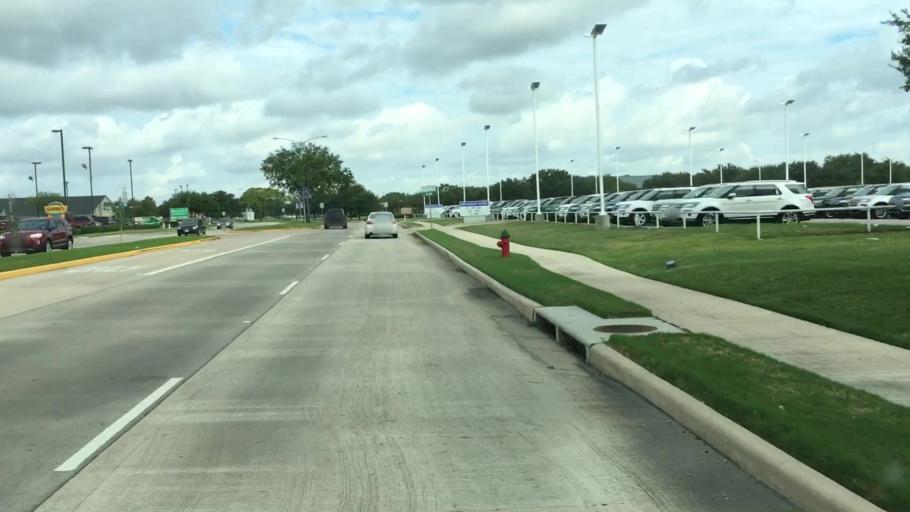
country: US
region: Texas
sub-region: Fort Bend County
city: Meadows Place
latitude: 29.6460
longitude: -95.5784
